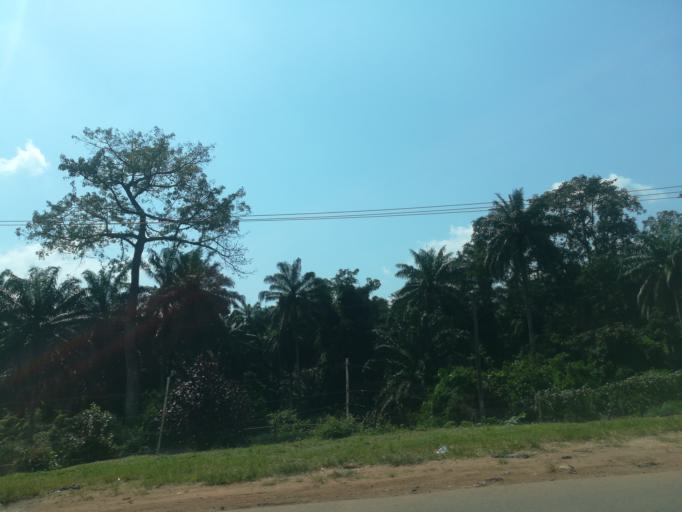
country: NG
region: Oyo
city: Moniya
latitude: 7.4976
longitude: 3.9135
